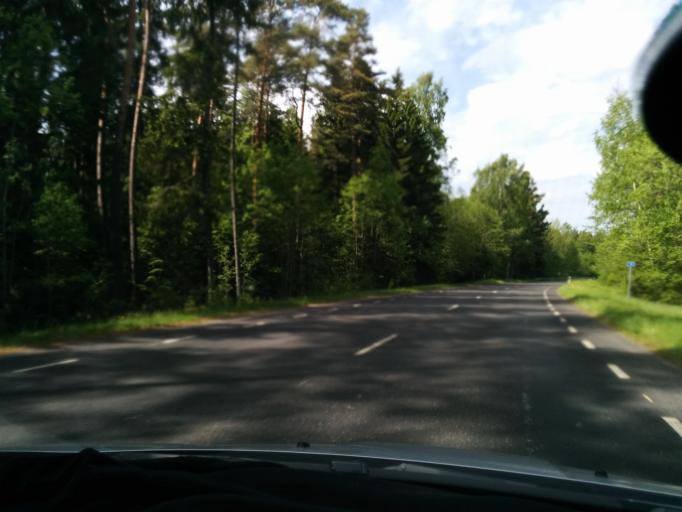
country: EE
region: Harju
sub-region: Loksa linn
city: Loksa
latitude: 59.5570
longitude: 25.7255
